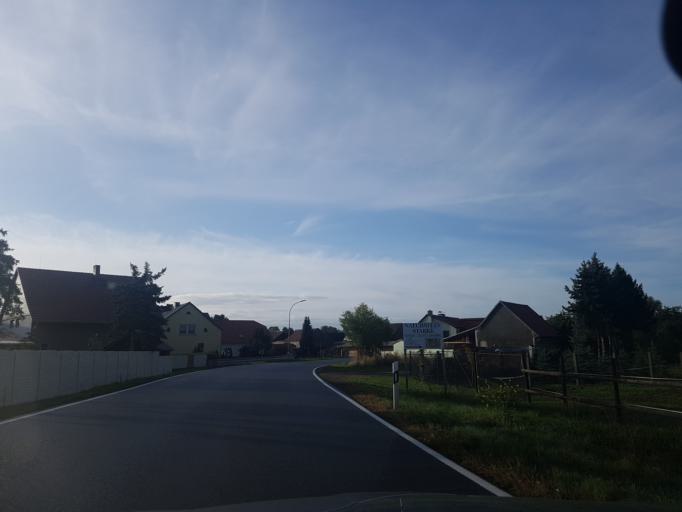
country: DE
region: Saxony
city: Arzberg
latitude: 51.6162
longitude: 13.1467
